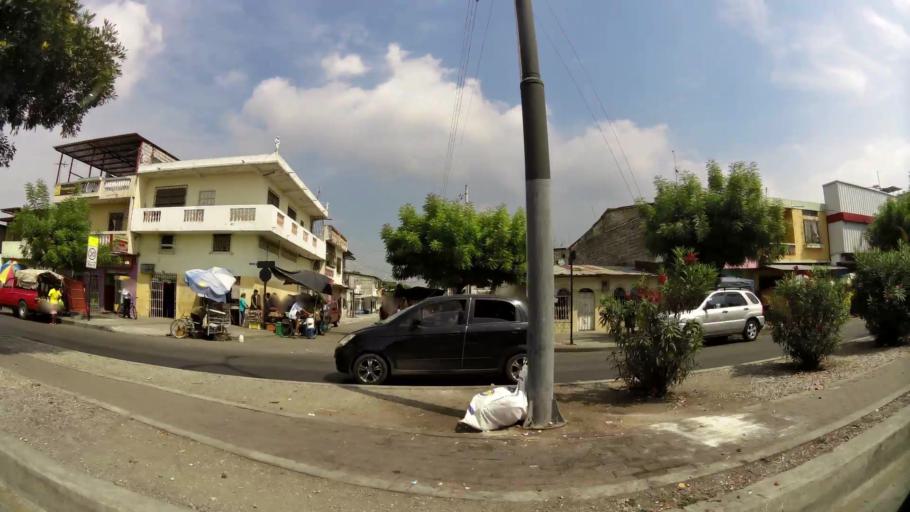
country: EC
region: Guayas
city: Guayaquil
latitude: -2.2620
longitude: -79.8783
